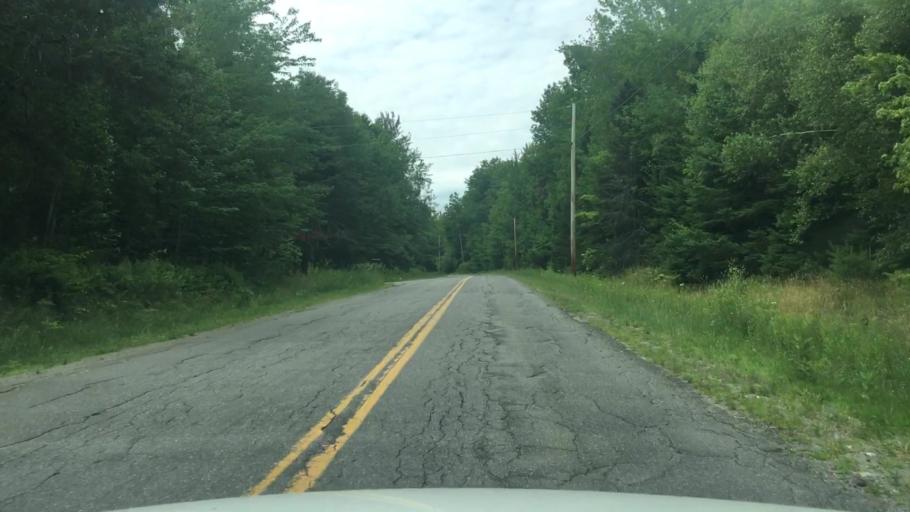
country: US
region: Maine
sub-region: Kennebec County
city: Albion
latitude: 44.5023
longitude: -69.3623
